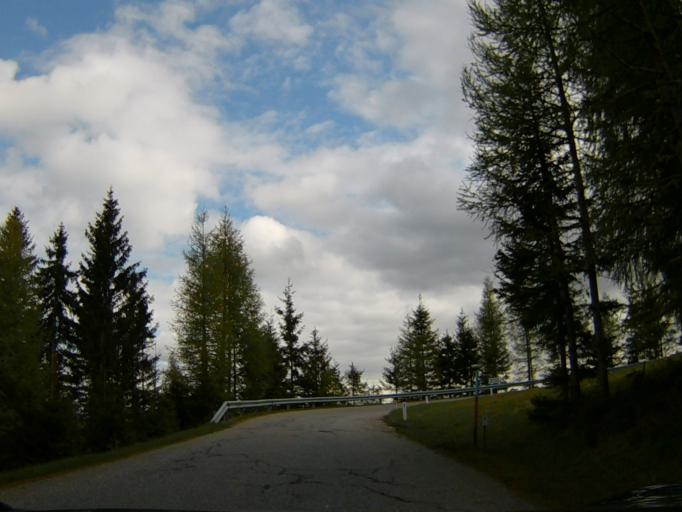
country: AT
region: Carinthia
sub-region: Politischer Bezirk Villach Land
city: Stockenboi
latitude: 46.7421
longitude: 13.5275
